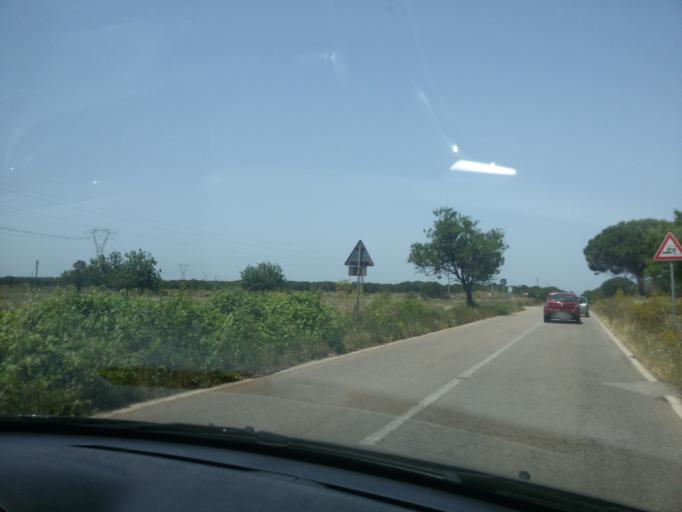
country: IT
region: Apulia
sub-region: Provincia di Brindisi
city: San Pancrazio Salentino
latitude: 40.3445
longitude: 17.8476
